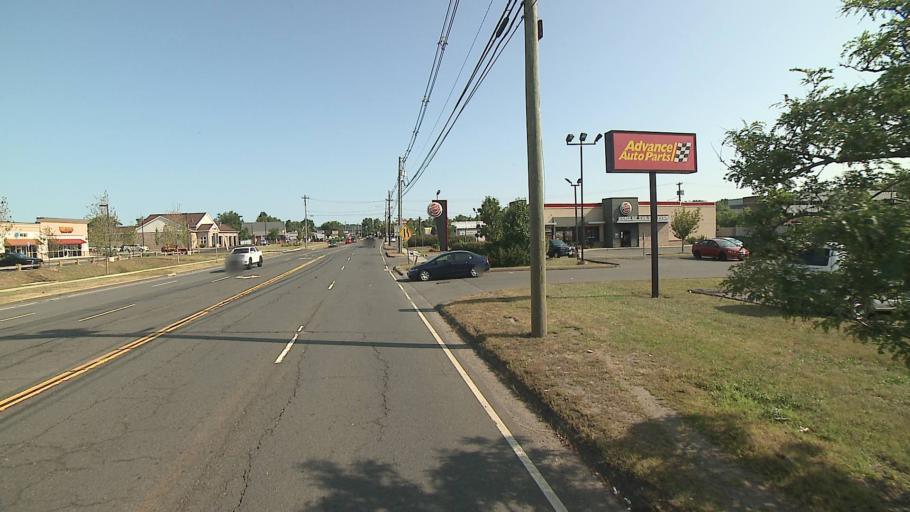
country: US
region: Connecticut
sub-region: New Haven County
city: Wallingford
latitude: 41.4813
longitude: -72.8104
